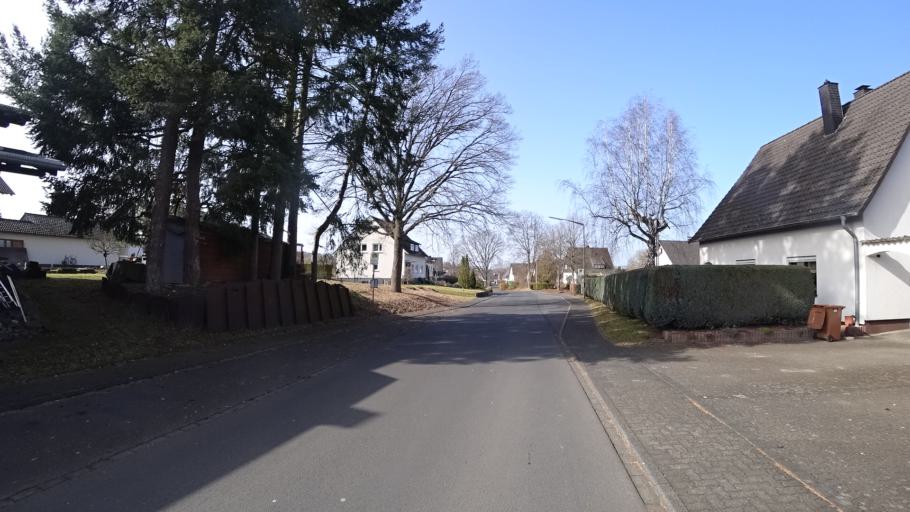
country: DE
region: Rheinland-Pfalz
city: Wissen
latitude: 50.7749
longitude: 7.7589
